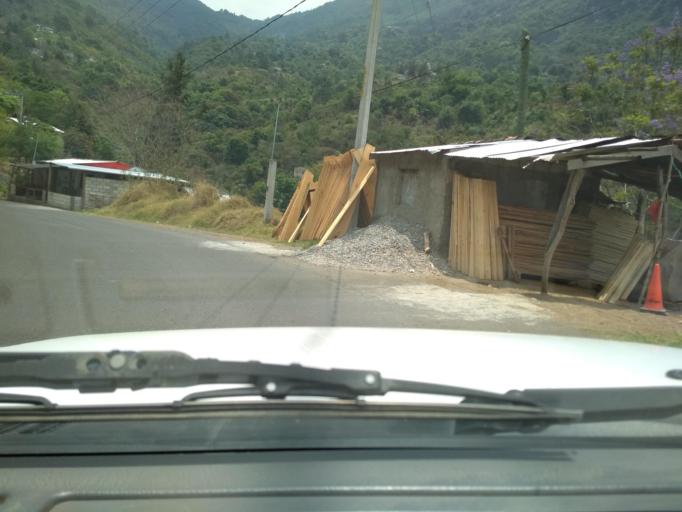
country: MX
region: Veracruz
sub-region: Camerino Z. Mendoza
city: La Cuesta
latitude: 18.7958
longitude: -97.1750
